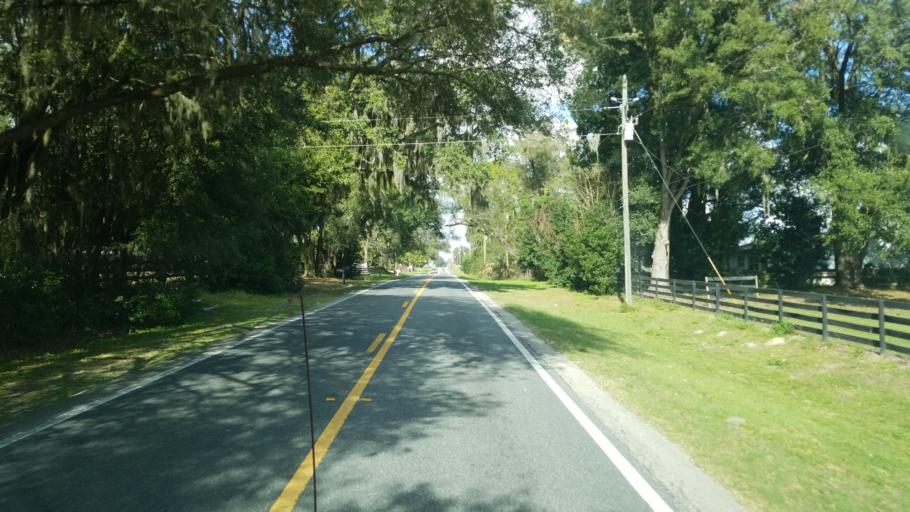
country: US
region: Florida
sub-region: Marion County
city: Belleview
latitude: 28.9779
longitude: -82.1200
